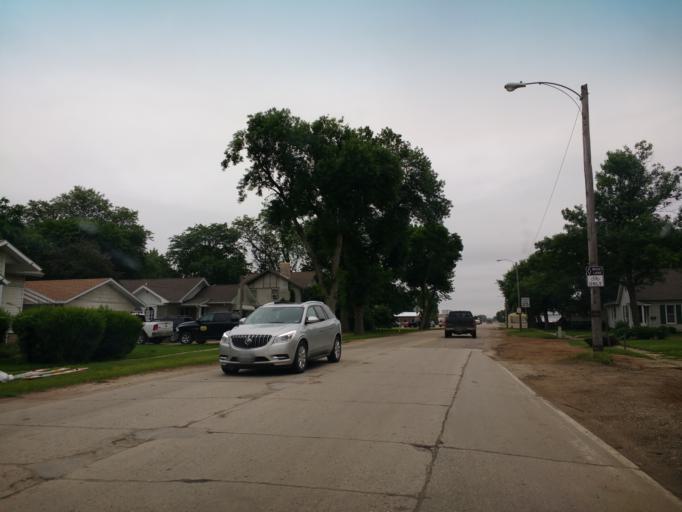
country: US
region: Iowa
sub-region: Dickinson County
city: Milford
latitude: 43.3279
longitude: -95.1498
